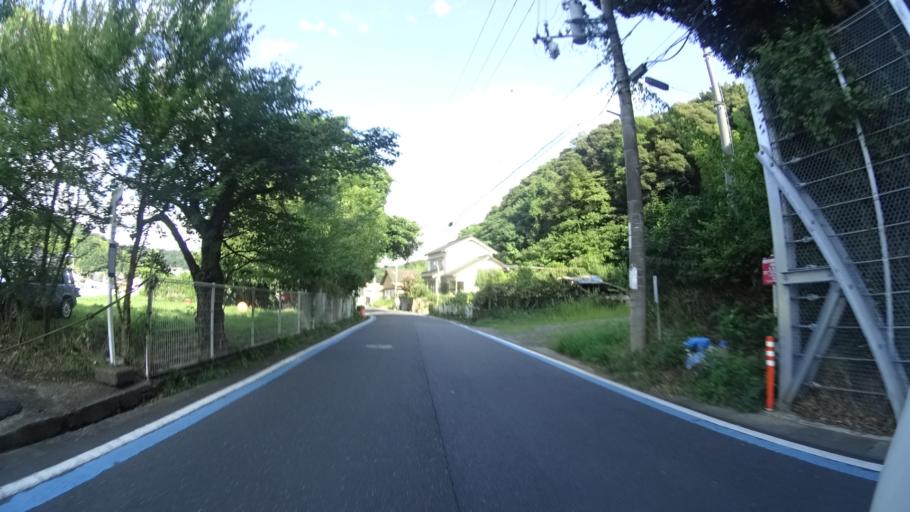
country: JP
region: Kyoto
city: Maizuru
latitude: 35.4749
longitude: 135.3451
